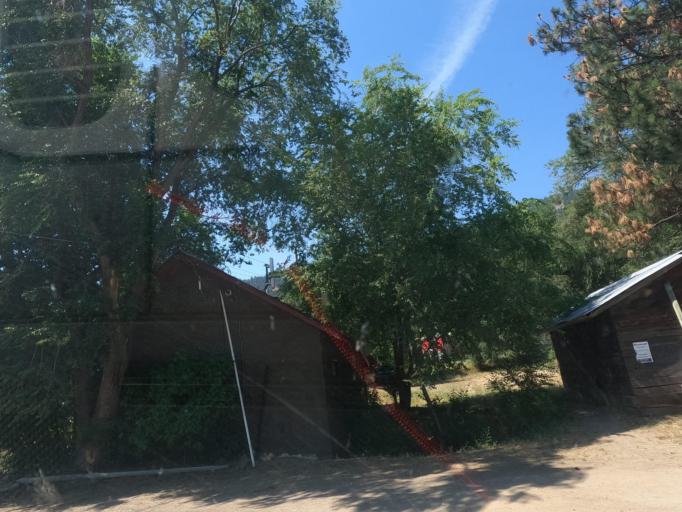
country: CA
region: British Columbia
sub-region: Regional District of North Okanagan
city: Vernon
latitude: 50.1107
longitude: -119.3859
